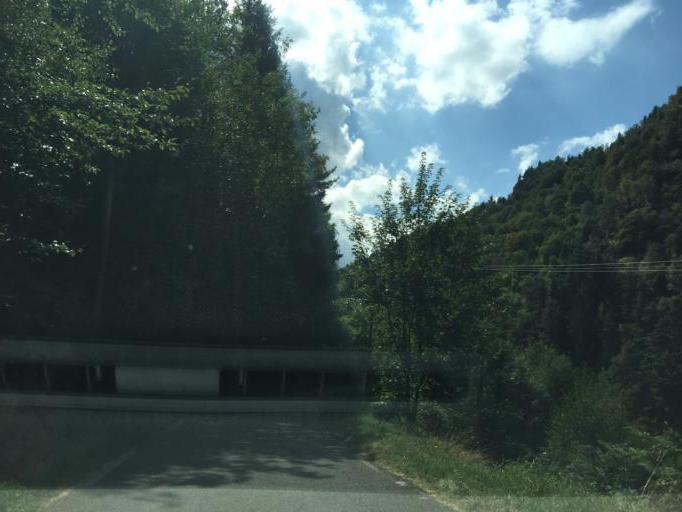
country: FR
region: Rhone-Alpes
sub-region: Departement de la Loire
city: Saint-Jean-Bonnefonds
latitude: 45.3983
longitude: 4.4476
